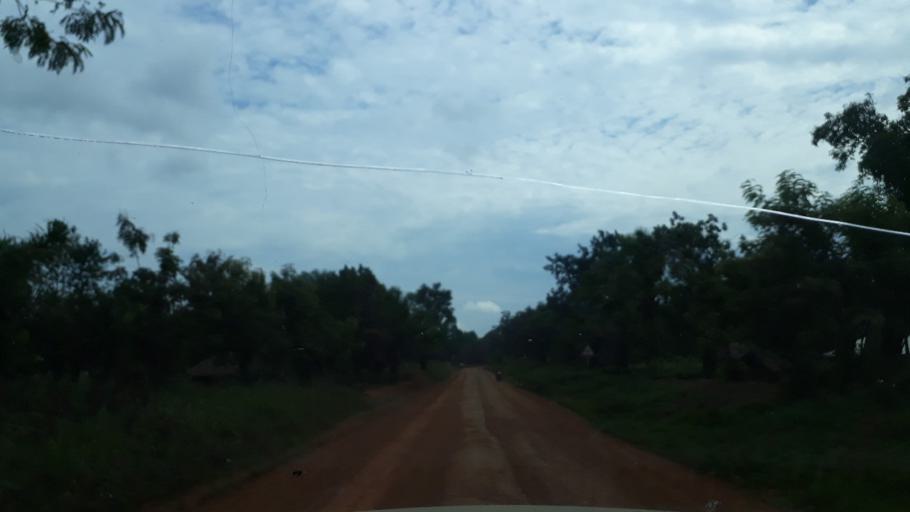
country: CD
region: Eastern Province
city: Bunia
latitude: 1.4556
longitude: 30.0161
